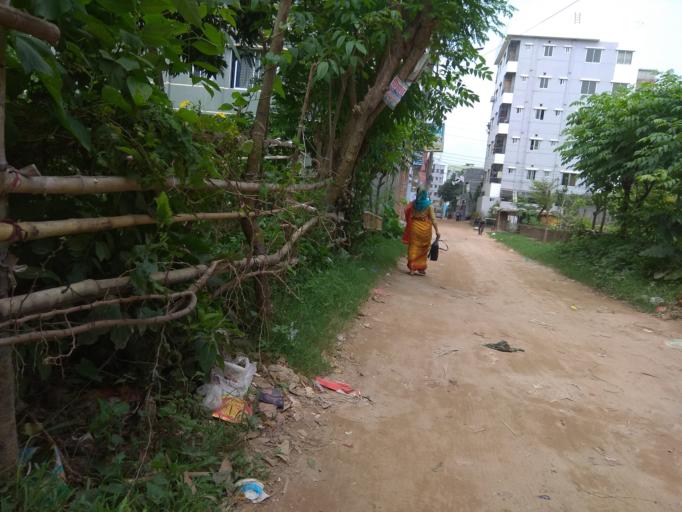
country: BD
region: Dhaka
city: Tungi
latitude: 23.8280
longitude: 90.3519
